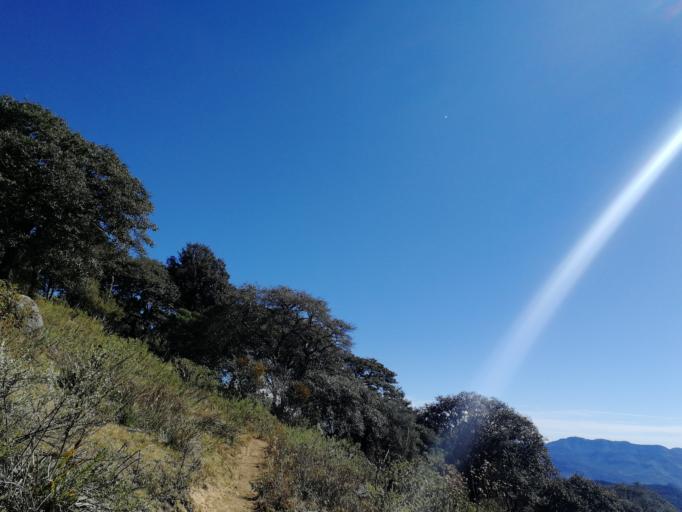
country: MX
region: San Luis Potosi
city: Zaragoza
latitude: 22.0098
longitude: -100.6188
